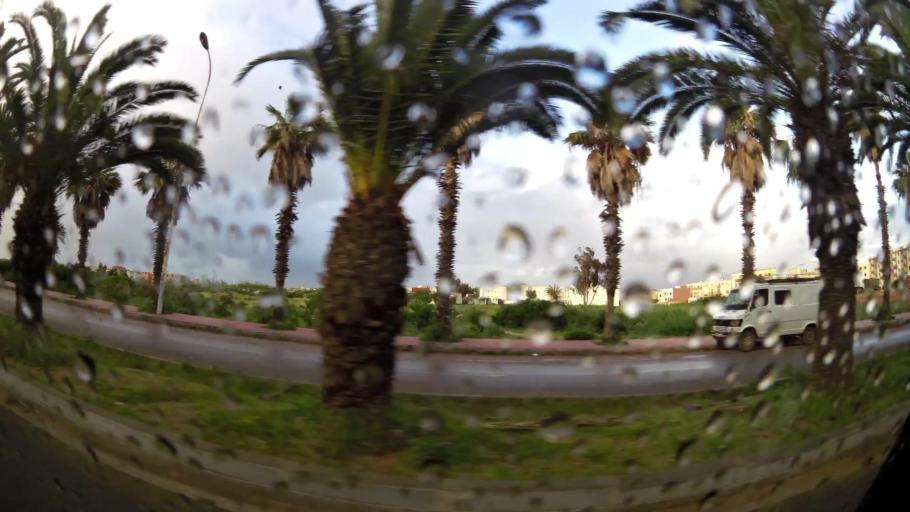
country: MA
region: Doukkala-Abda
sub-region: El-Jadida
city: El Jadida
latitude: 33.2307
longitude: -8.4893
